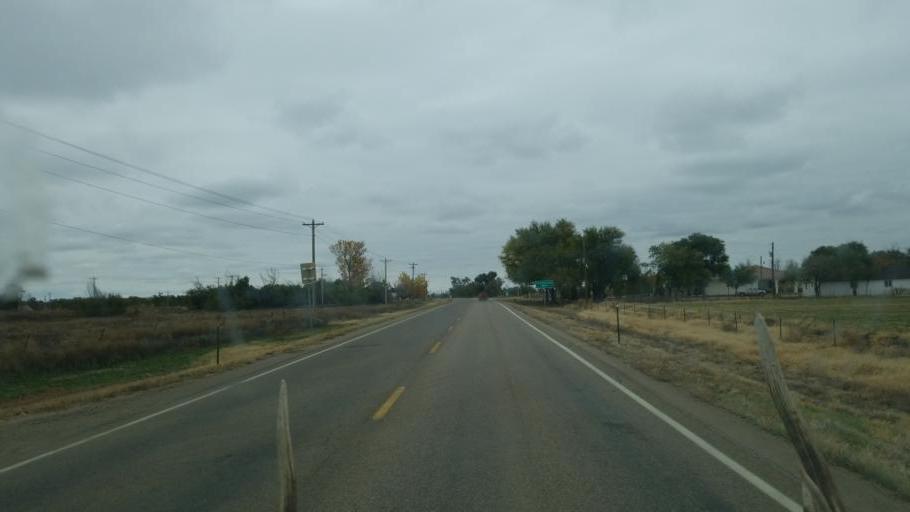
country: US
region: Colorado
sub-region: Crowley County
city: Ordway
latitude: 38.2121
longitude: -103.7686
